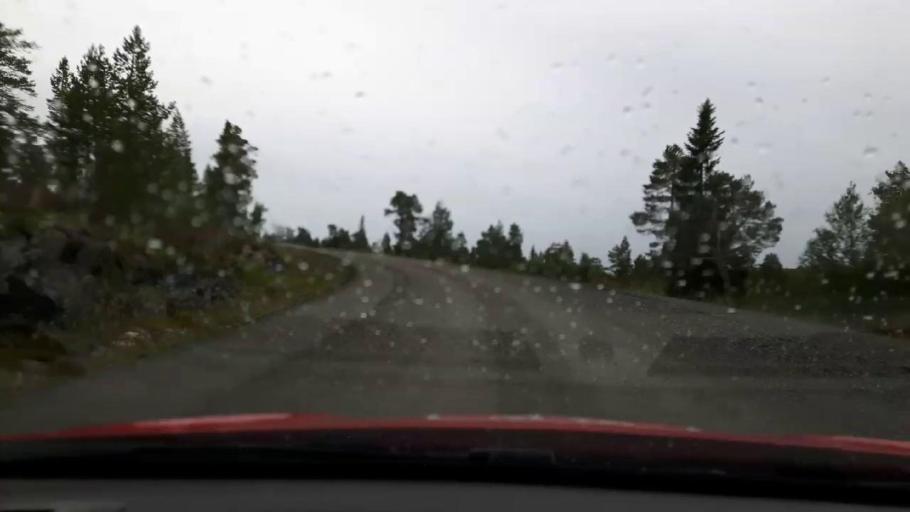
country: NO
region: Nord-Trondelag
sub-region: Meraker
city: Meraker
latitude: 63.6399
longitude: 12.2732
